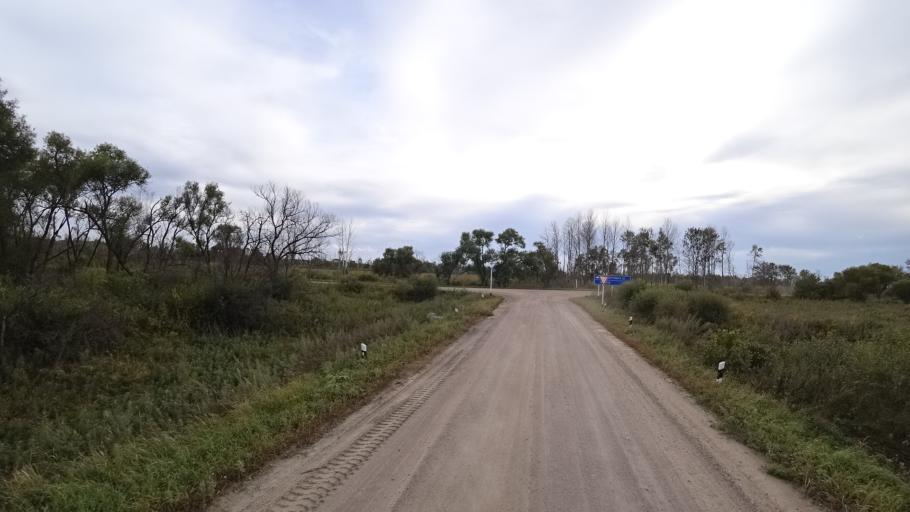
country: RU
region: Amur
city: Arkhara
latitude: 49.3737
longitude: 130.2056
